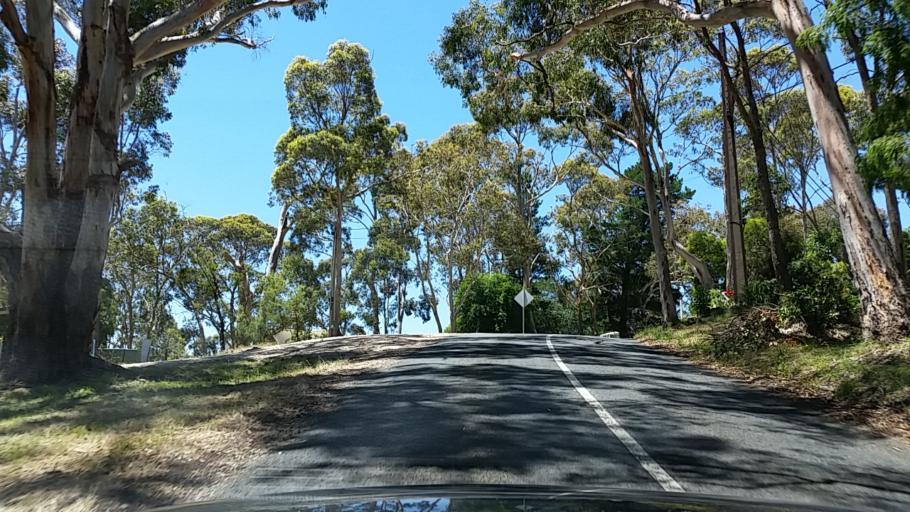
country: AU
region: South Australia
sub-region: Adelaide Hills
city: Crafers
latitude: -35.0002
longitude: 138.6846
